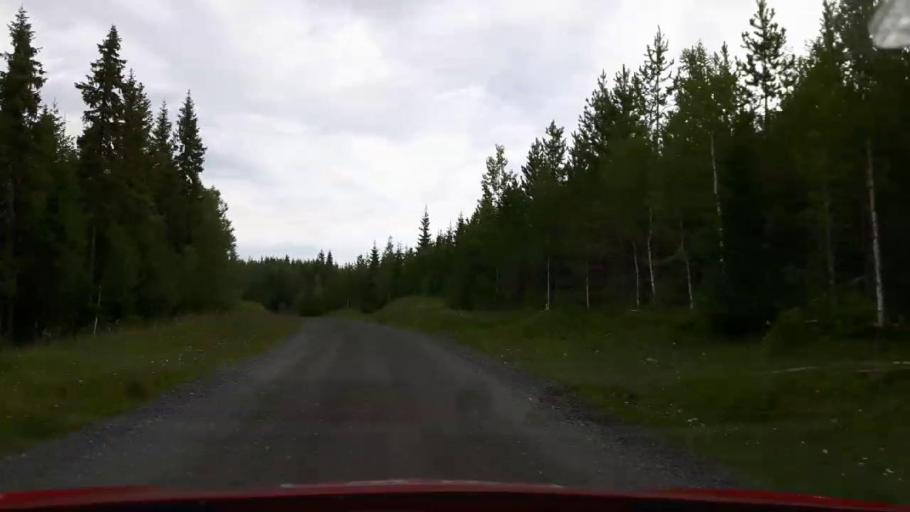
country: SE
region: Jaemtland
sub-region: OEstersunds Kommun
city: Lit
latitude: 63.3999
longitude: 15.2302
